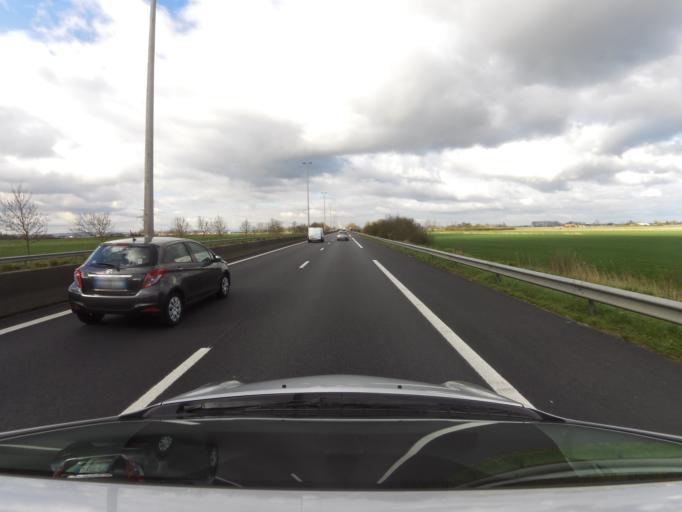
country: FR
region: Nord-Pas-de-Calais
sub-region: Departement du Pas-de-Calais
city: Vieille-Eglise
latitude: 50.9436
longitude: 2.0955
